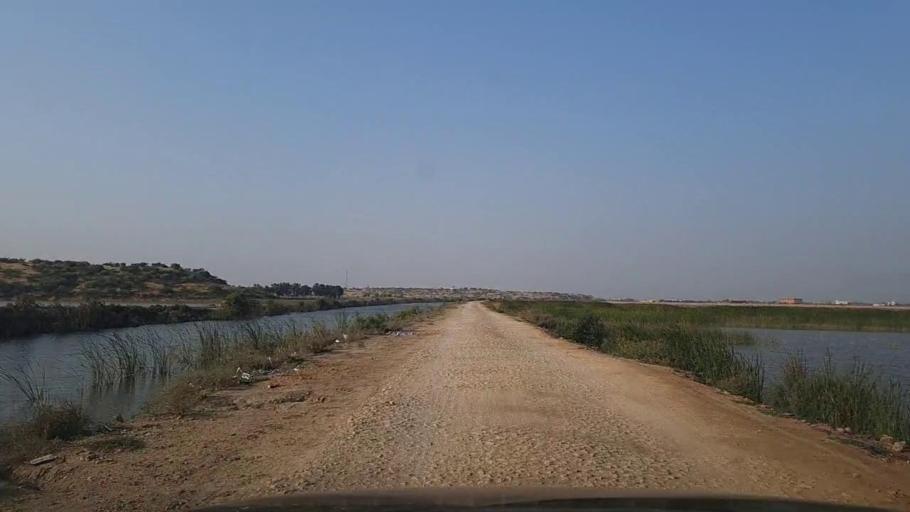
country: PK
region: Sindh
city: Thatta
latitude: 24.7327
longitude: 67.9071
